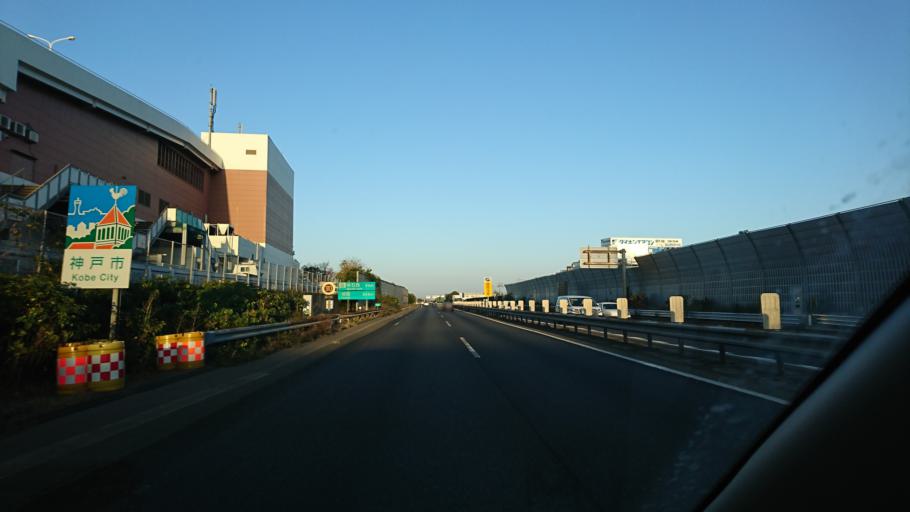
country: JP
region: Hyogo
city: Akashi
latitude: 34.7115
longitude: 134.9410
